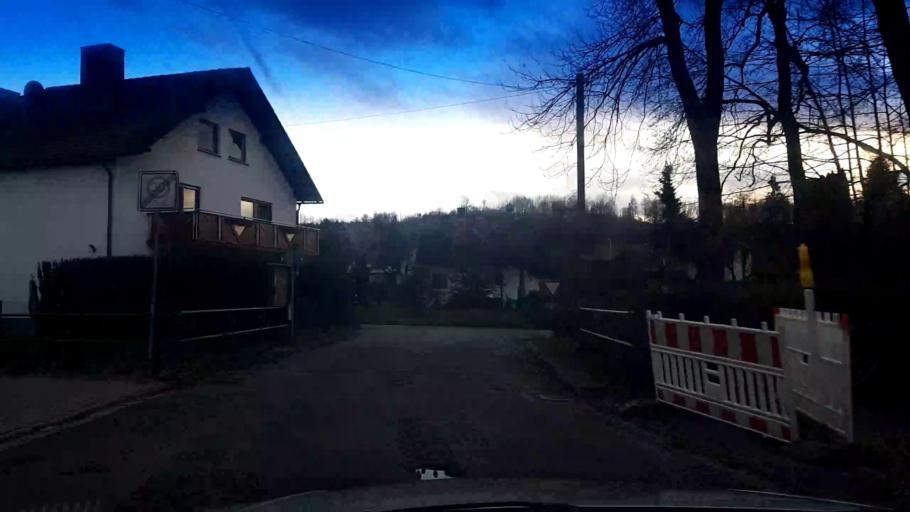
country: DE
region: Bavaria
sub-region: Upper Franconia
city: Buttenheim
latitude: 49.8076
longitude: 11.0547
